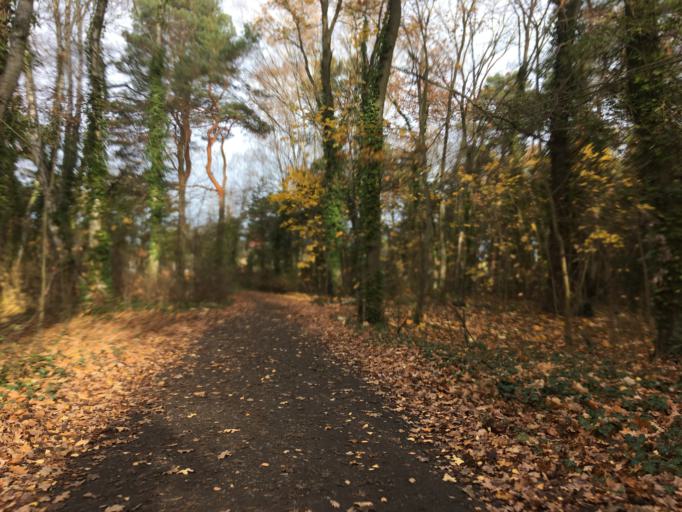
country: DE
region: Berlin
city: Adlershof
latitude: 52.4473
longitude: 13.5397
